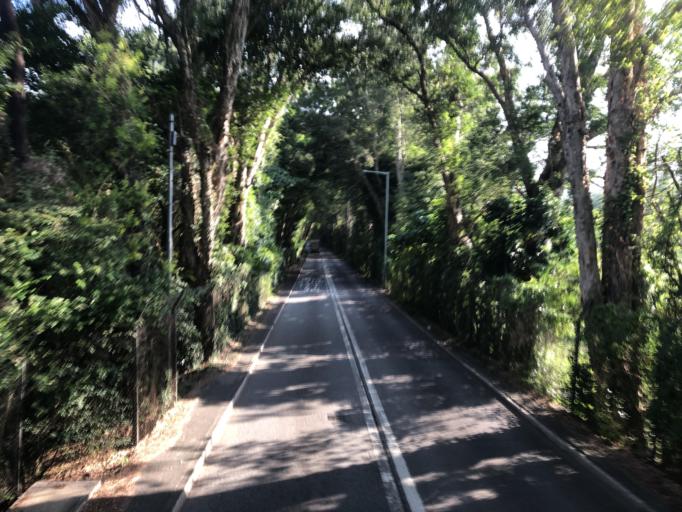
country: HK
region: Tai Po
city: Tai Po
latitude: 22.4950
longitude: 114.1208
